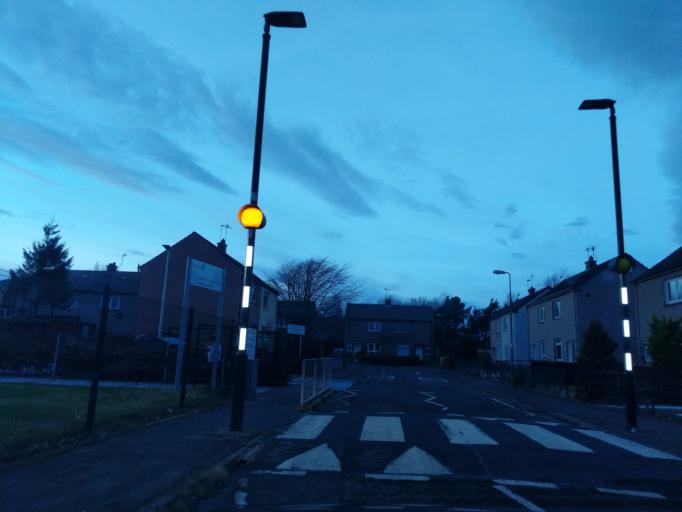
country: GB
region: Scotland
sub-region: Midlothian
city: Loanhead
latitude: 55.8697
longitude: -3.1830
